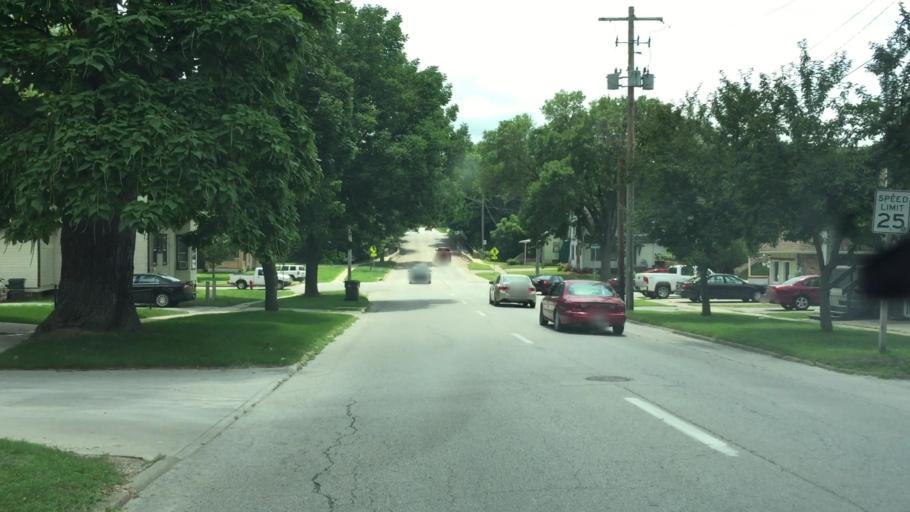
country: US
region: Iowa
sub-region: Johnson County
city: Iowa City
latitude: 41.6619
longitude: -91.5258
